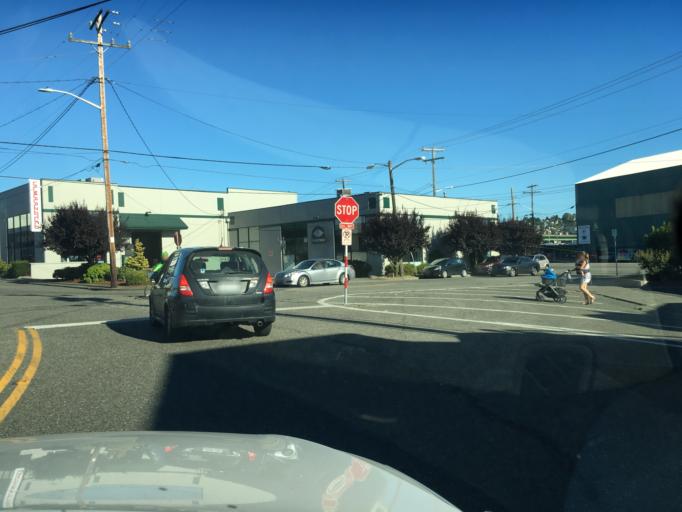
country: US
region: Washington
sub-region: King County
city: Seattle
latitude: 47.6630
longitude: -122.3792
